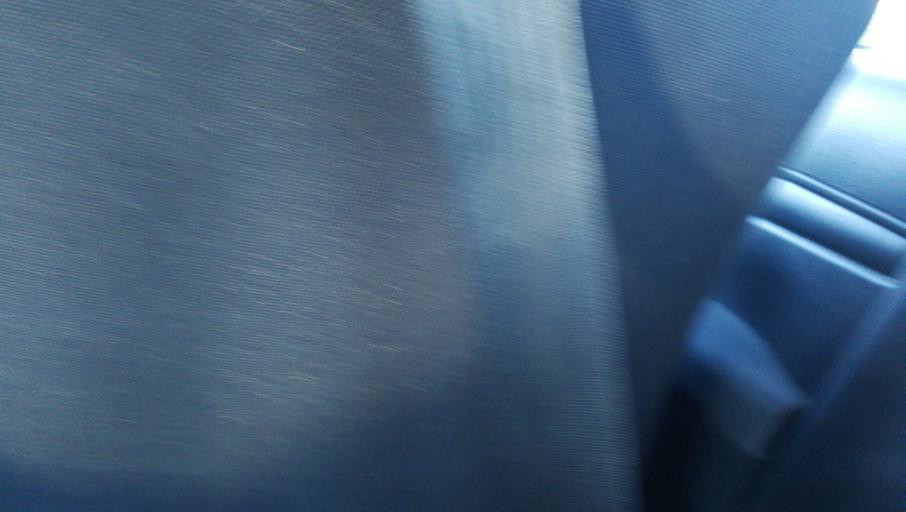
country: ET
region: Amhara
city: Were Ilu
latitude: 10.4842
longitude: 39.3019
